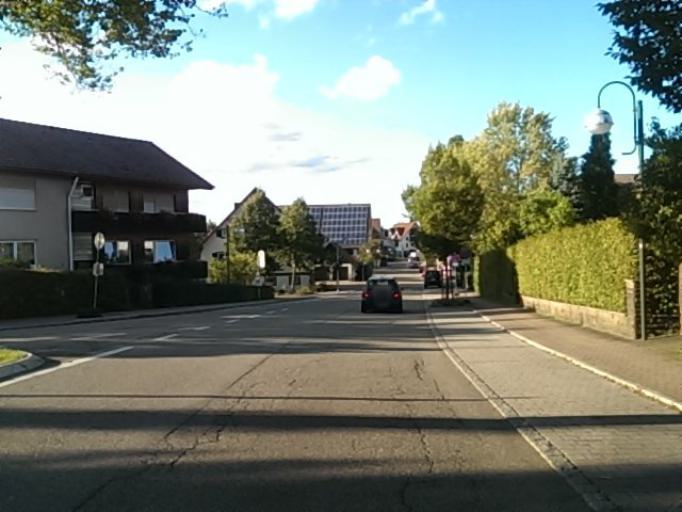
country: DE
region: Baden-Wuerttemberg
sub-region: Karlsruhe Region
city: Lossburg
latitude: 48.4091
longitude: 8.4534
